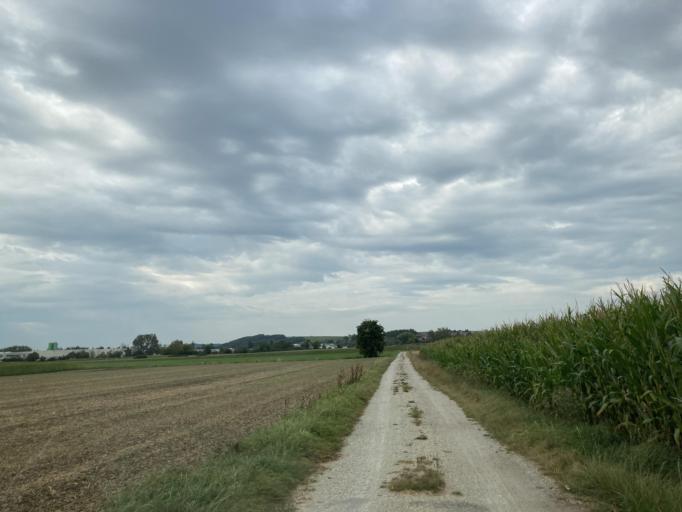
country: DE
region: Baden-Wuerttemberg
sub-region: Freiburg Region
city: Donaueschingen
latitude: 47.9253
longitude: 8.5478
